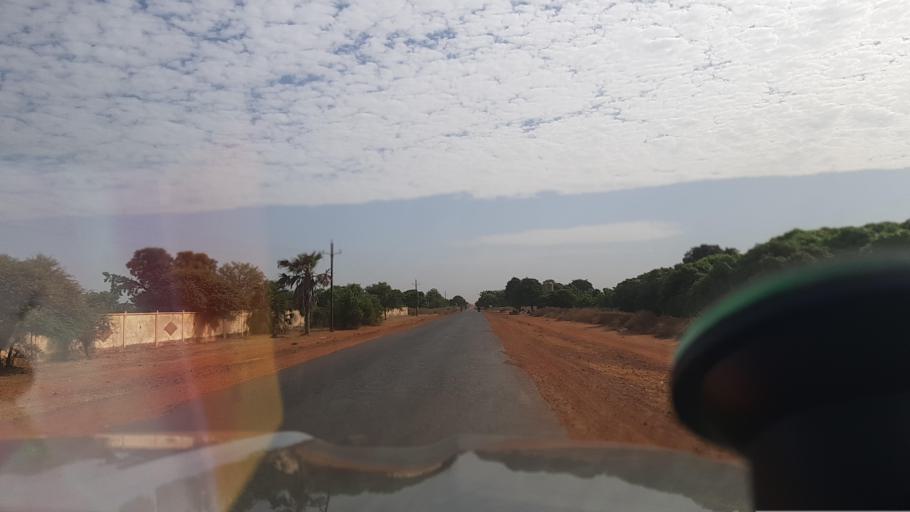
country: ML
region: Segou
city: Segou
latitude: 13.4988
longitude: -6.1566
